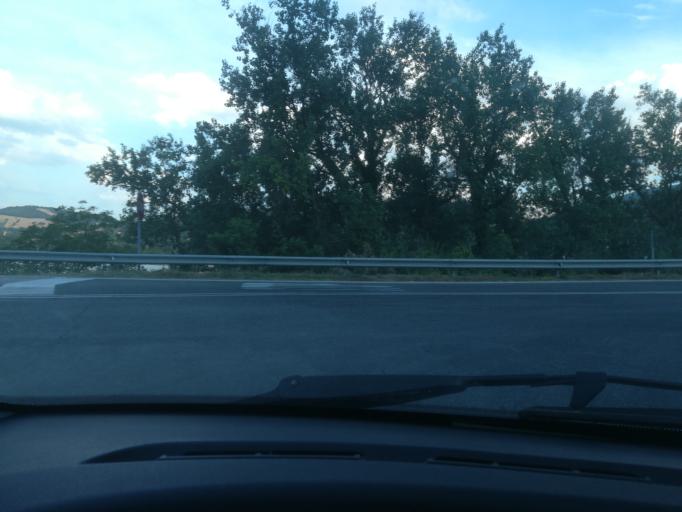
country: IT
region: The Marches
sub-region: Provincia di Macerata
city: Caldarola
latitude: 43.1457
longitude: 13.1988
